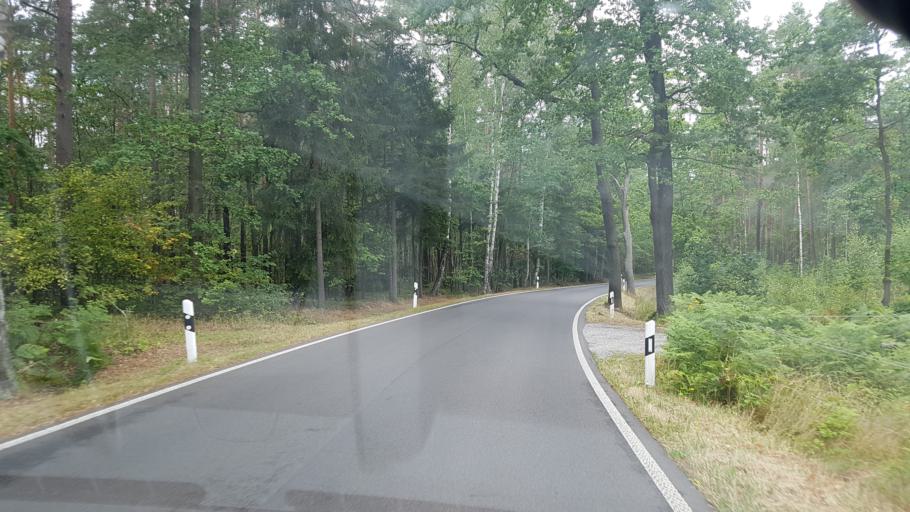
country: DE
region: Saxony
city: Mucka
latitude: 51.3777
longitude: 14.7094
